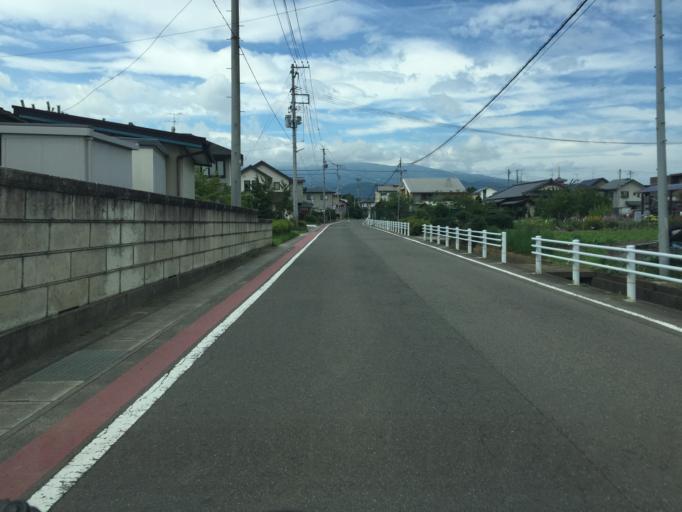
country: JP
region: Fukushima
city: Fukushima-shi
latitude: 37.7349
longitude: 140.4200
